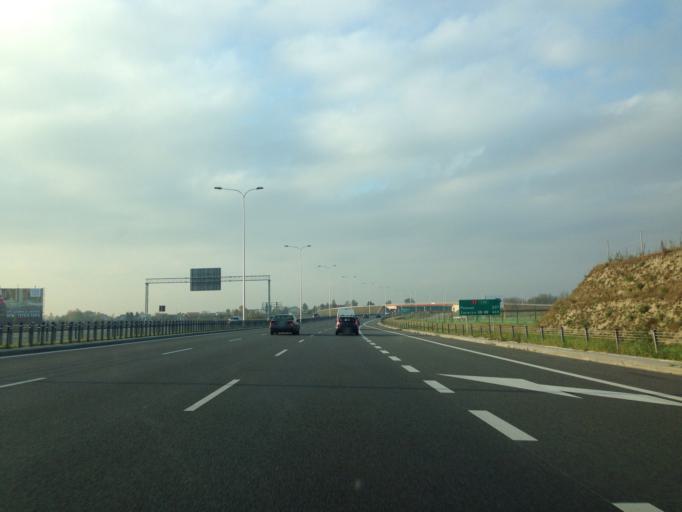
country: PL
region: Masovian Voivodeship
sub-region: Powiat pruszkowski
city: Rybie
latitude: 52.1427
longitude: 20.9686
